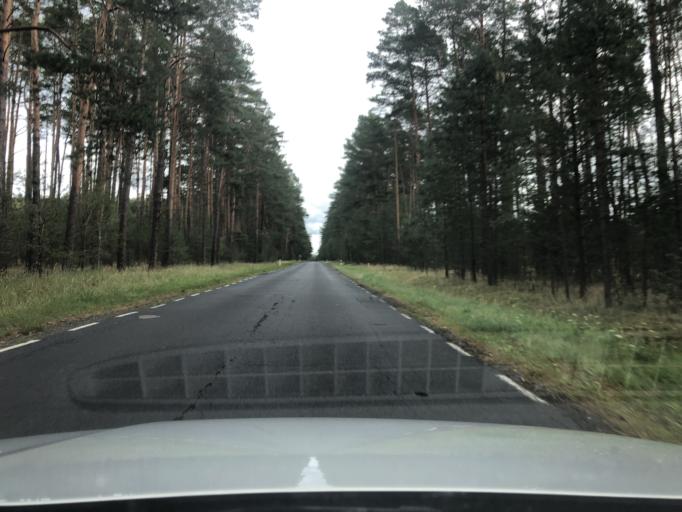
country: PL
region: Greater Poland Voivodeship
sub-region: Powiat czarnkowsko-trzcianecki
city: Krzyz Wielkopolski
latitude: 52.8580
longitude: 15.9315
